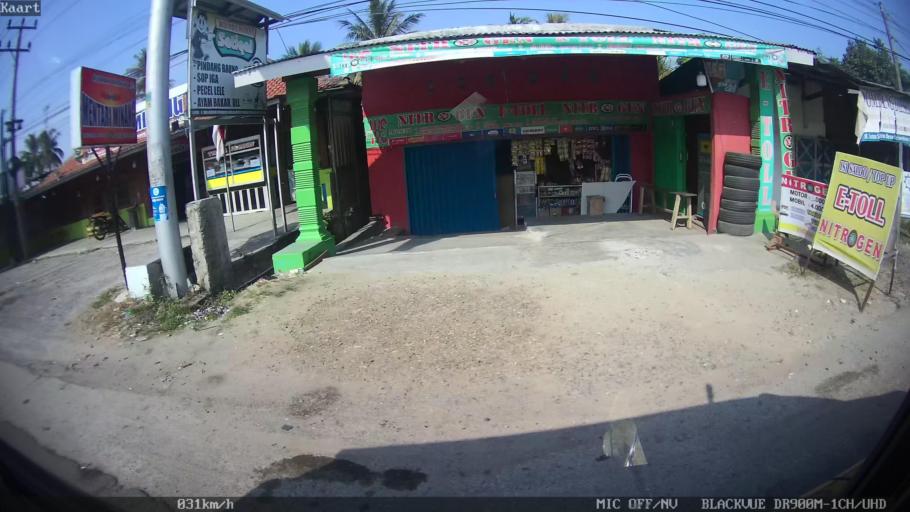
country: ID
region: Lampung
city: Natar
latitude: -5.2831
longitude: 105.1905
